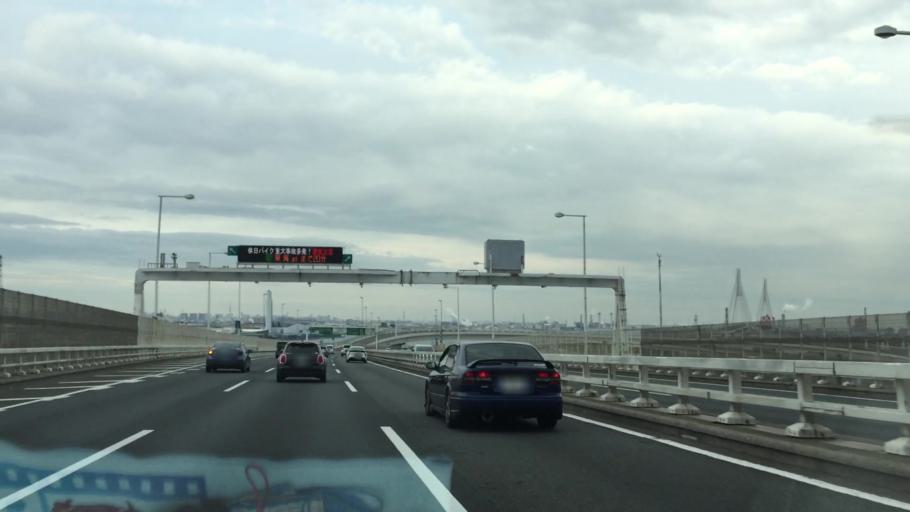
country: JP
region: Kanagawa
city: Yokohama
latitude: 35.4591
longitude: 139.6769
